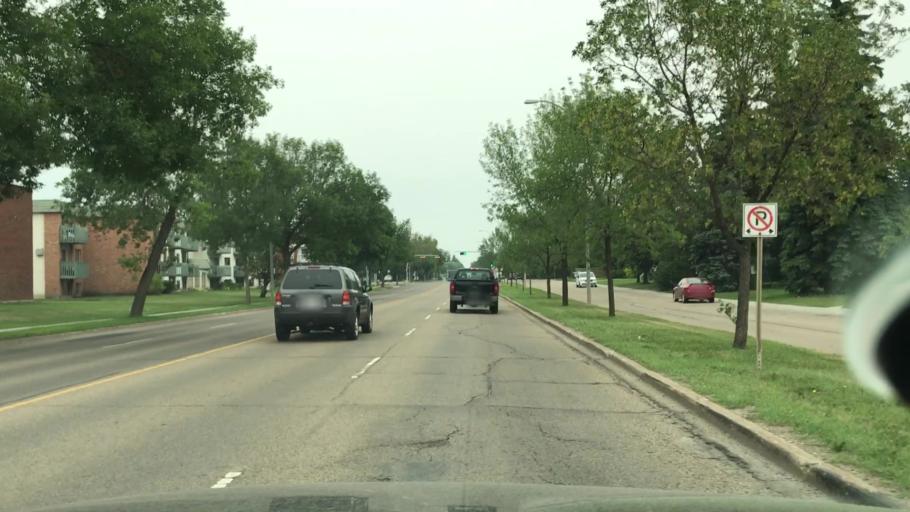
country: CA
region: Alberta
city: Edmonton
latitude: 53.5268
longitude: -113.5779
